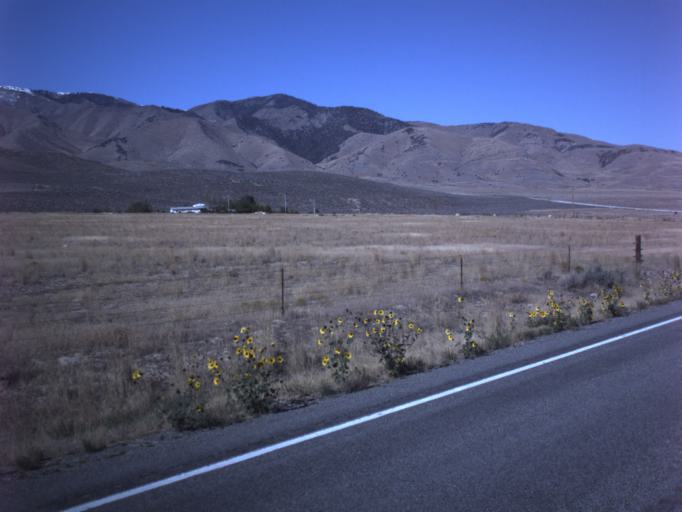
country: US
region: Utah
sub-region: Tooele County
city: Grantsville
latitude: 40.6346
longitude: -112.5176
